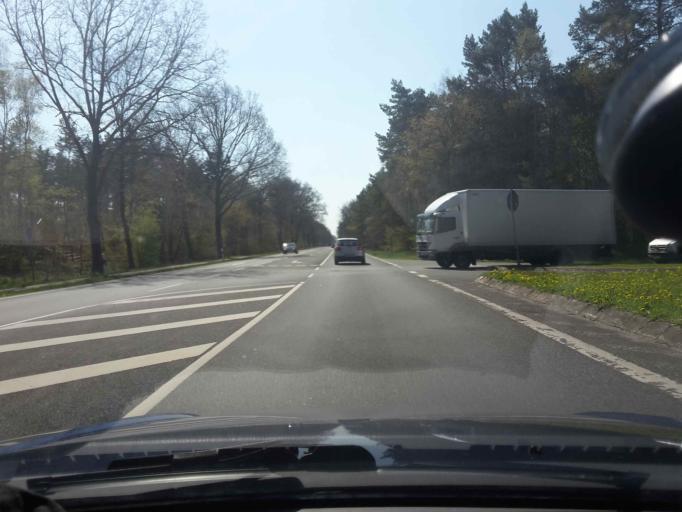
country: DE
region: Lower Saxony
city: Welle
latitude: 53.2031
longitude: 9.8245
